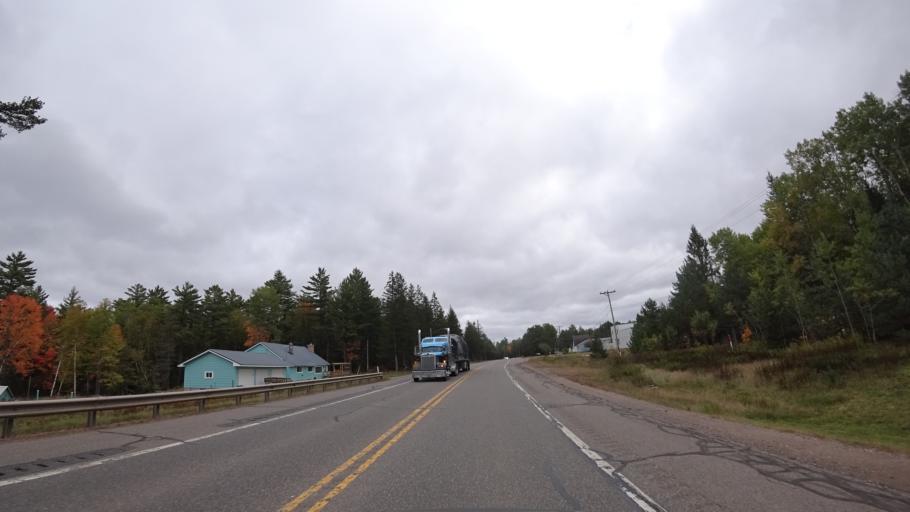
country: US
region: Michigan
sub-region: Marquette County
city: West Ishpeming
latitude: 46.4984
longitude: -87.9415
